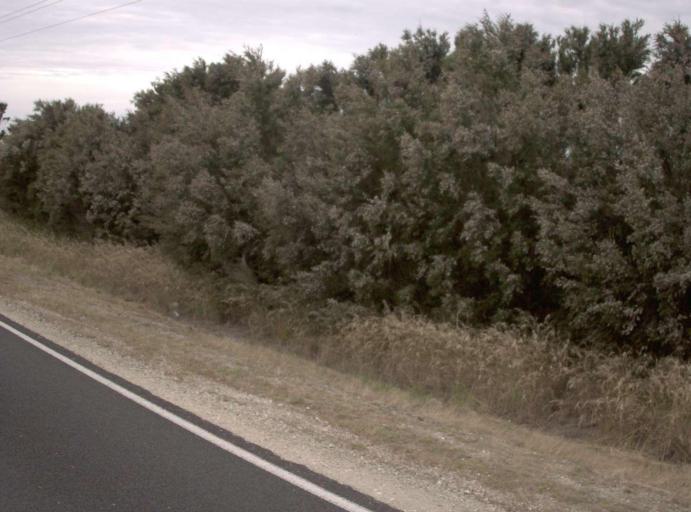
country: AU
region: Victoria
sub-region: Wellington
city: Sale
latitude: -38.2012
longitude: 147.3187
